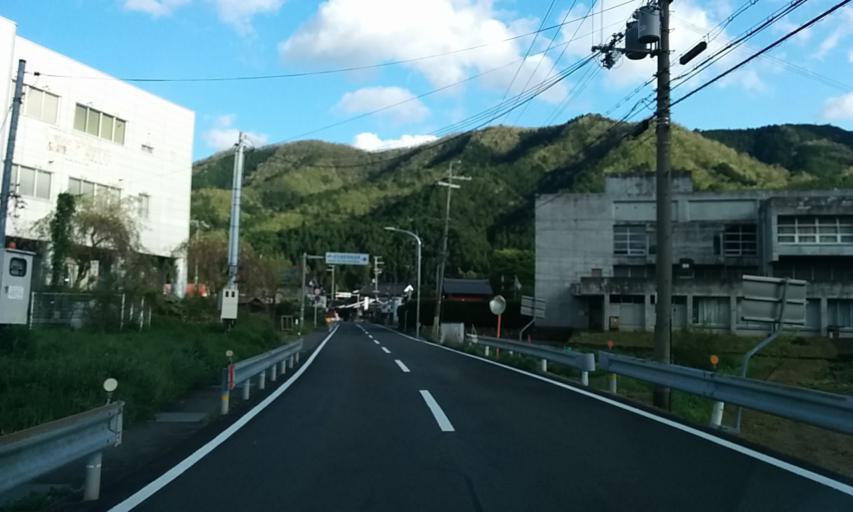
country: JP
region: Kyoto
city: Ayabe
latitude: 35.2611
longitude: 135.3965
